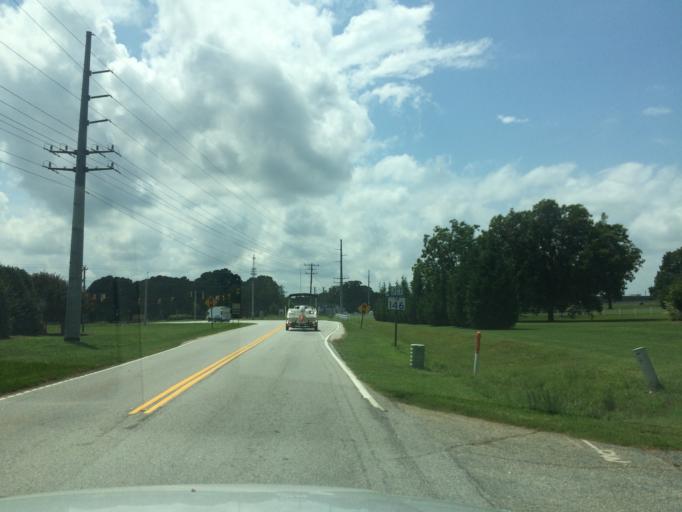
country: US
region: South Carolina
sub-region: Greenville County
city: Five Forks
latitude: 34.8082
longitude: -82.2171
